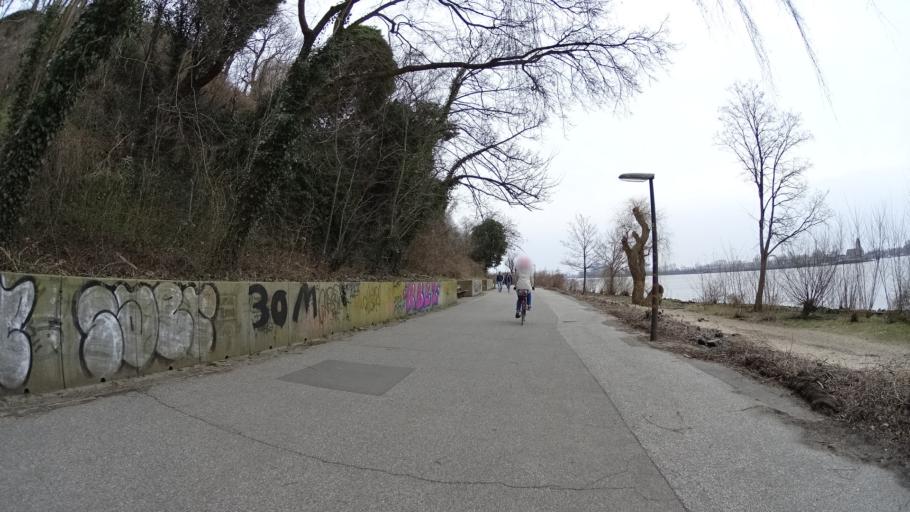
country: DE
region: Hamburg
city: Altona
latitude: 53.5461
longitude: 9.8748
